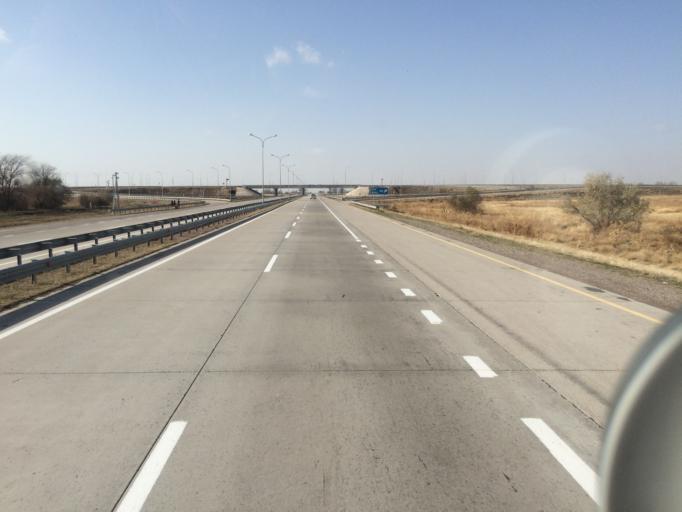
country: KZ
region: Zhambyl
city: Oytal
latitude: 42.9281
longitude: 73.2479
